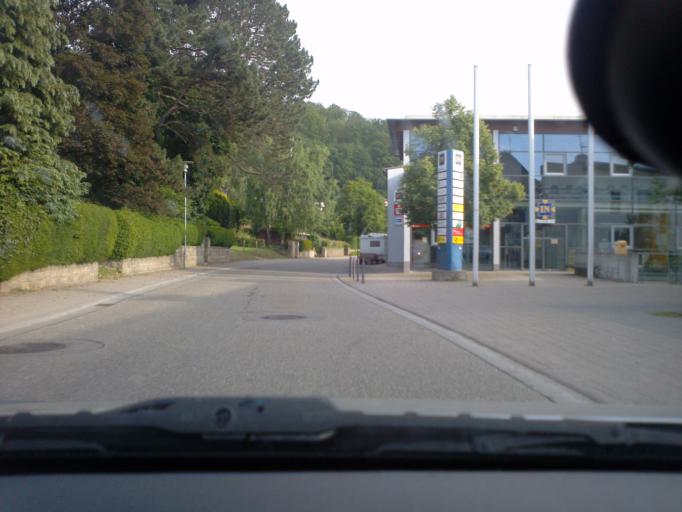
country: DE
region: Baden-Wuerttemberg
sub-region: Karlsruhe Region
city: Sternenfels
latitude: 49.0490
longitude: 8.8499
